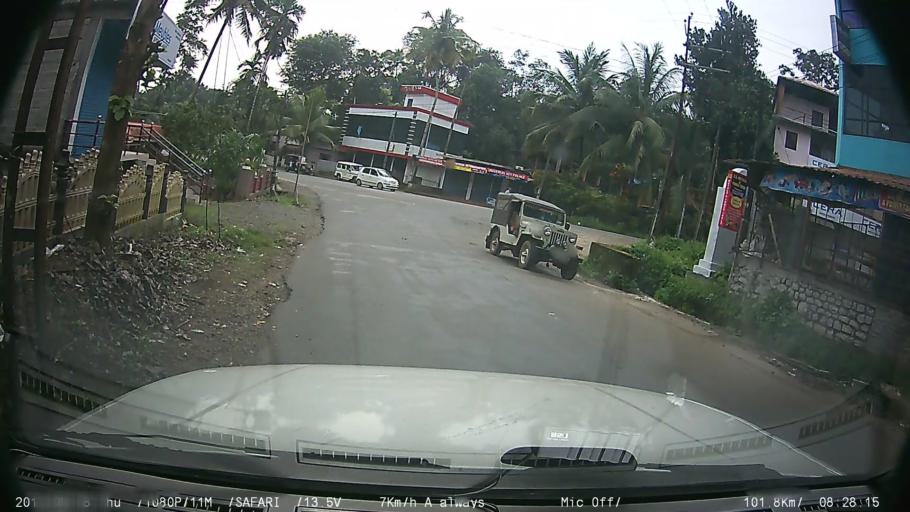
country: IN
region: Kerala
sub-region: Kottayam
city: Palackattumala
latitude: 9.6849
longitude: 76.6123
